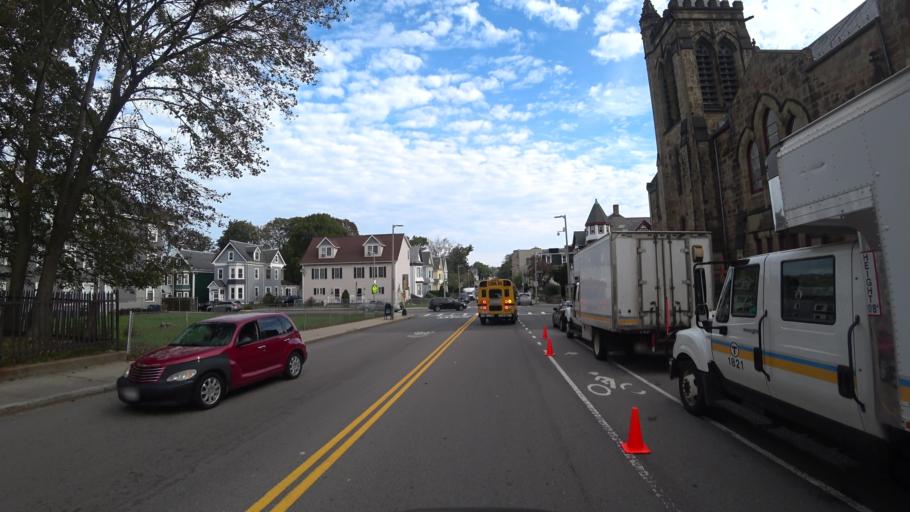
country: US
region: Massachusetts
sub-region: Suffolk County
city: Jamaica Plain
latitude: 42.3210
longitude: -71.0859
